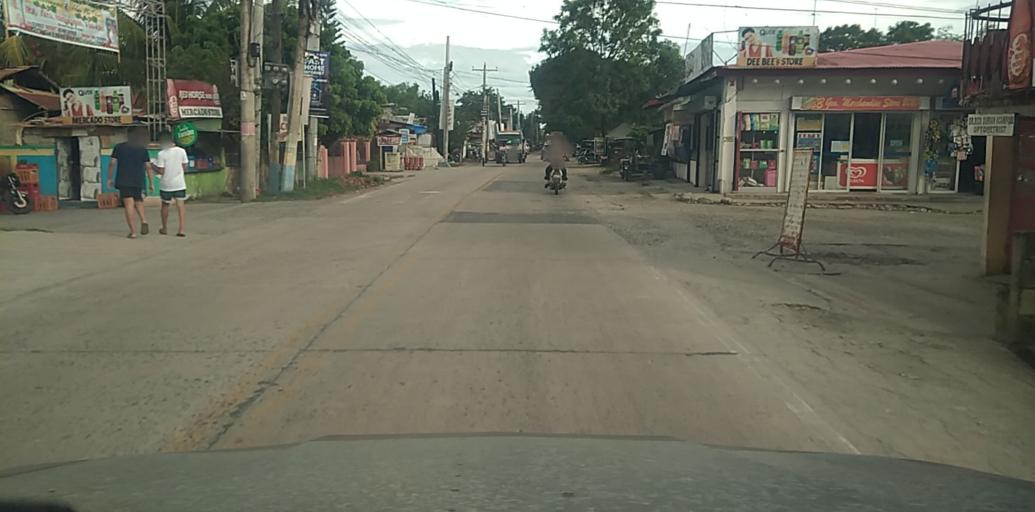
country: PH
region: Central Luzon
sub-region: Province of Pampanga
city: Arayat
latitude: 15.1516
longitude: 120.7421
